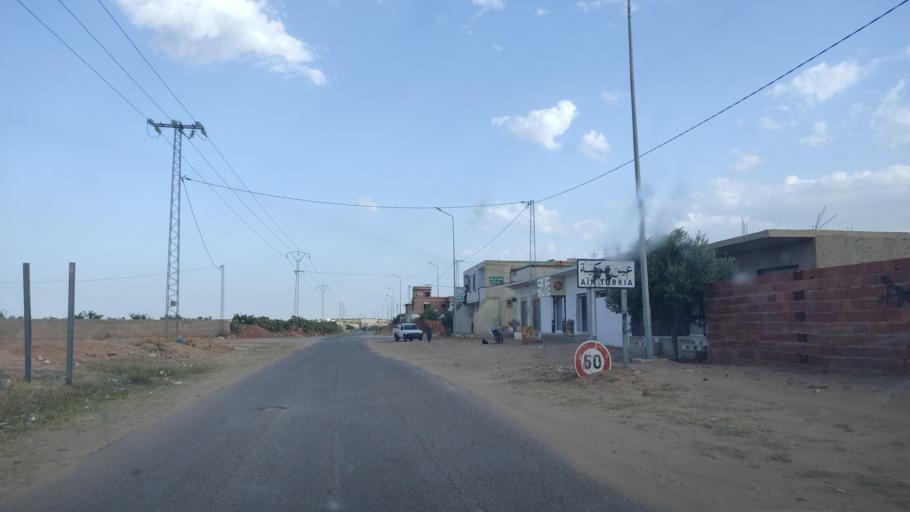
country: TN
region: Safaqis
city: Sfax
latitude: 34.8503
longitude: 10.6119
